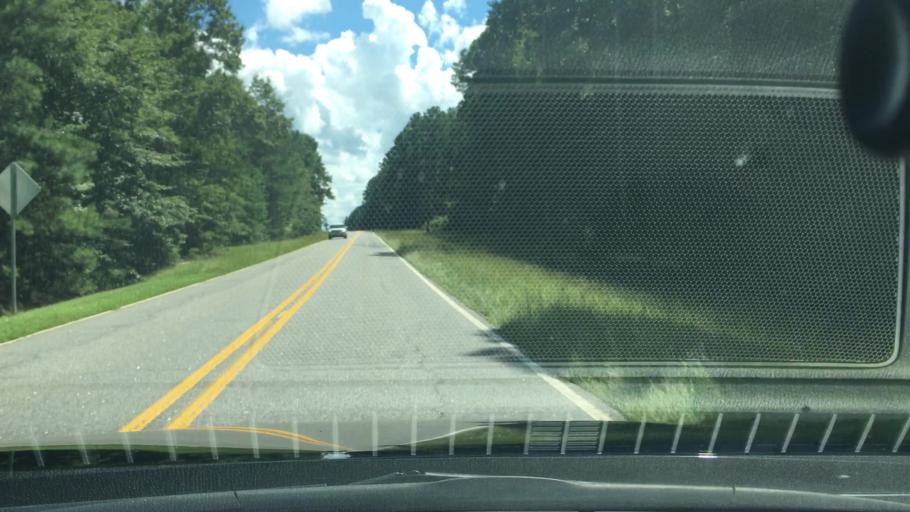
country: US
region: Georgia
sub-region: Putnam County
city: Jefferson
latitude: 33.3746
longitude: -83.2513
